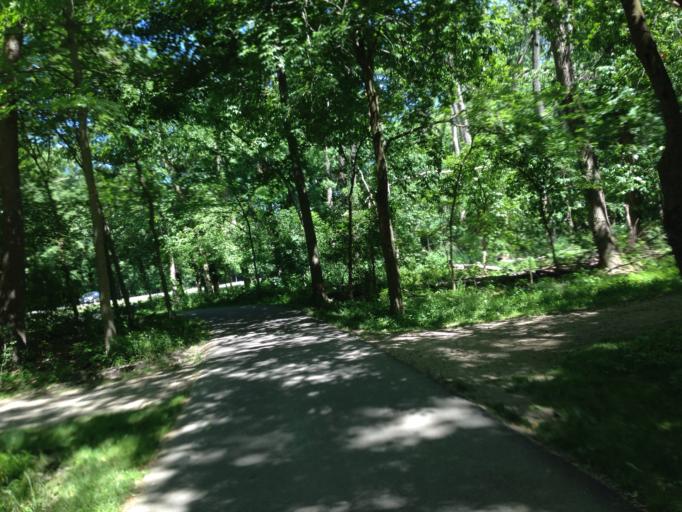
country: US
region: Ohio
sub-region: Cuyahoga County
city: Berea
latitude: 41.3467
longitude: -81.8398
